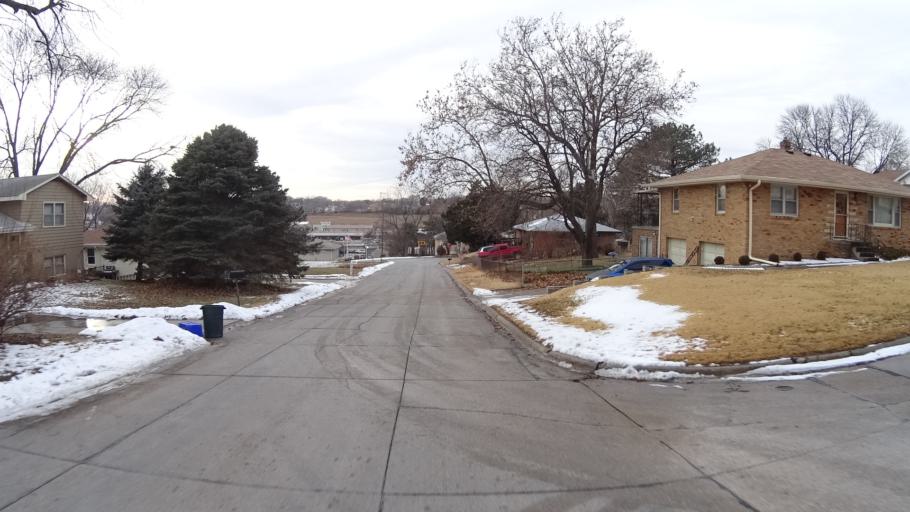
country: US
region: Nebraska
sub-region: Sarpy County
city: Bellevue
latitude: 41.1726
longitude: -95.9221
